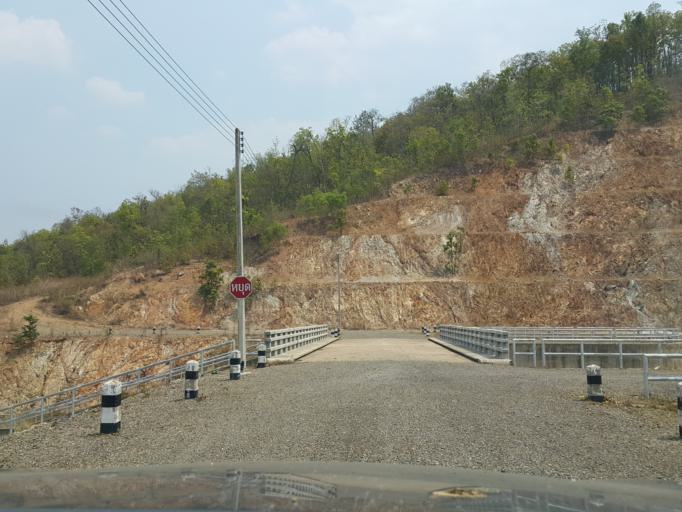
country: TH
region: Lampang
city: Mae Phrik
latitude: 17.4995
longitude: 99.0688
